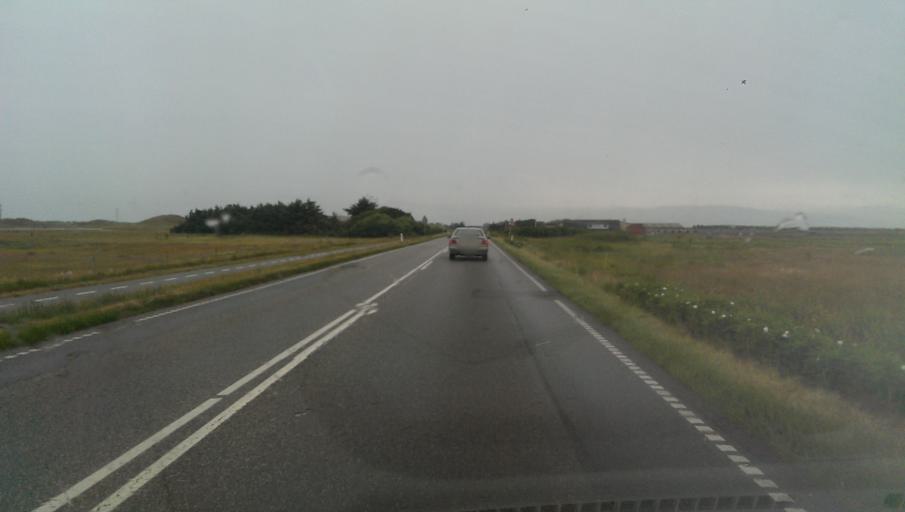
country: DK
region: Central Jutland
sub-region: Ringkobing-Skjern Kommune
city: Hvide Sande
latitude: 56.0303
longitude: 8.1190
